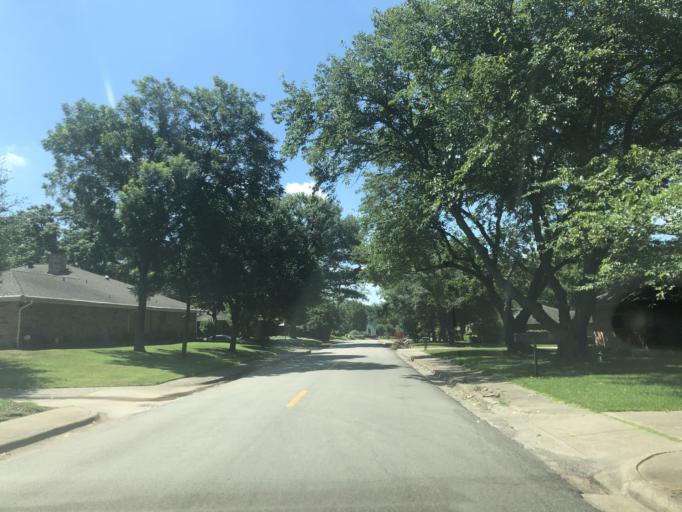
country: US
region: Texas
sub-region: Dallas County
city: Duncanville
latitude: 32.6510
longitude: -96.9294
